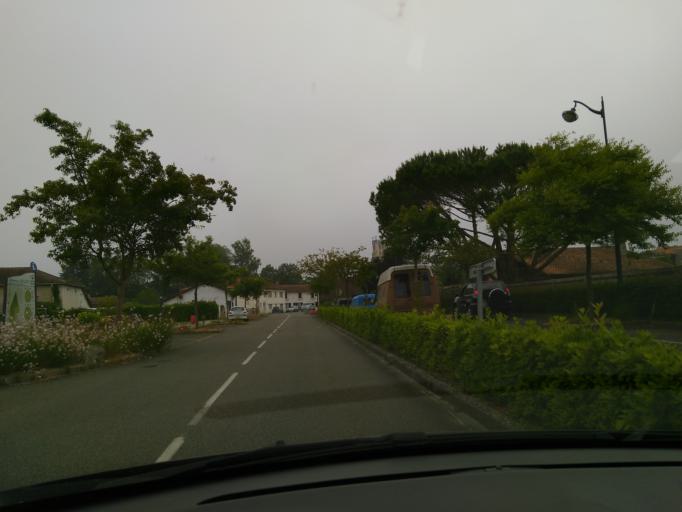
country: FR
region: Aquitaine
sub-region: Departement des Landes
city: Saint-Vincent-de-Paul
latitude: 43.7822
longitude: -0.9925
